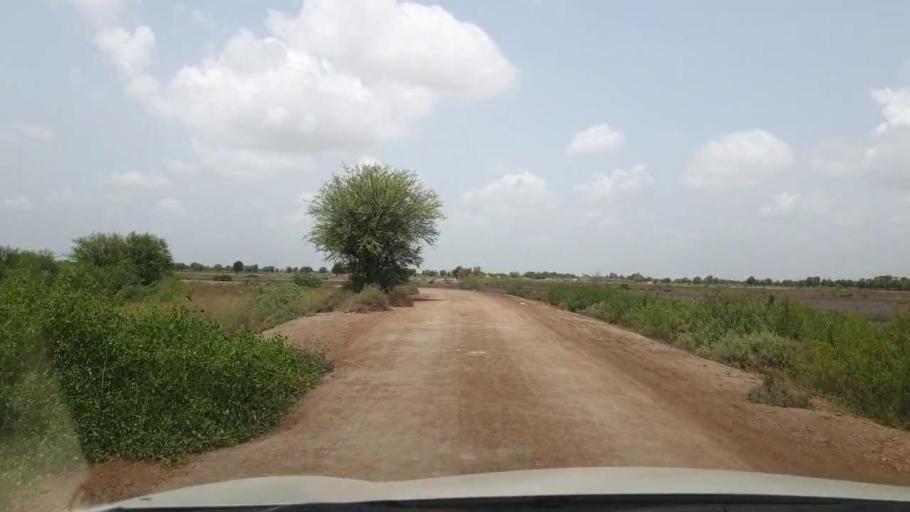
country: PK
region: Sindh
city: Chambar
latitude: 25.2100
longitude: 68.7682
